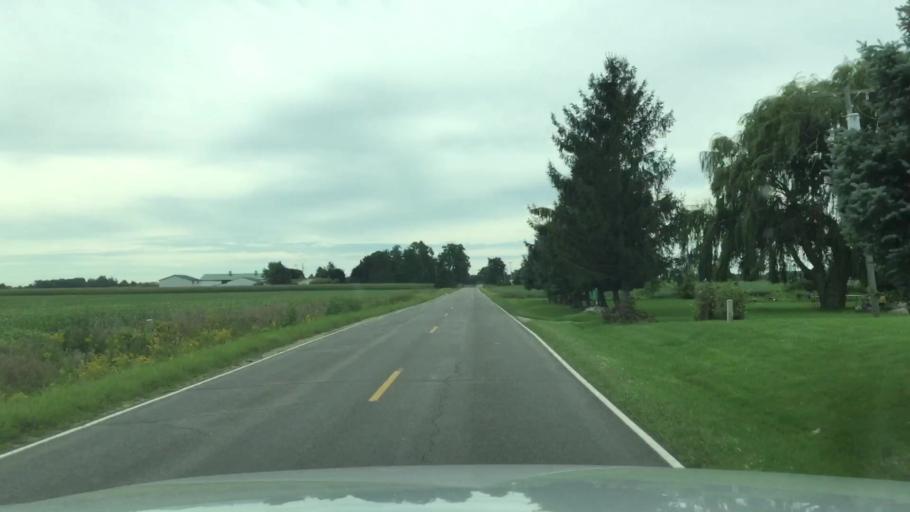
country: US
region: Michigan
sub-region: Shiawassee County
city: Durand
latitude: 43.0256
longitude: -83.9872
